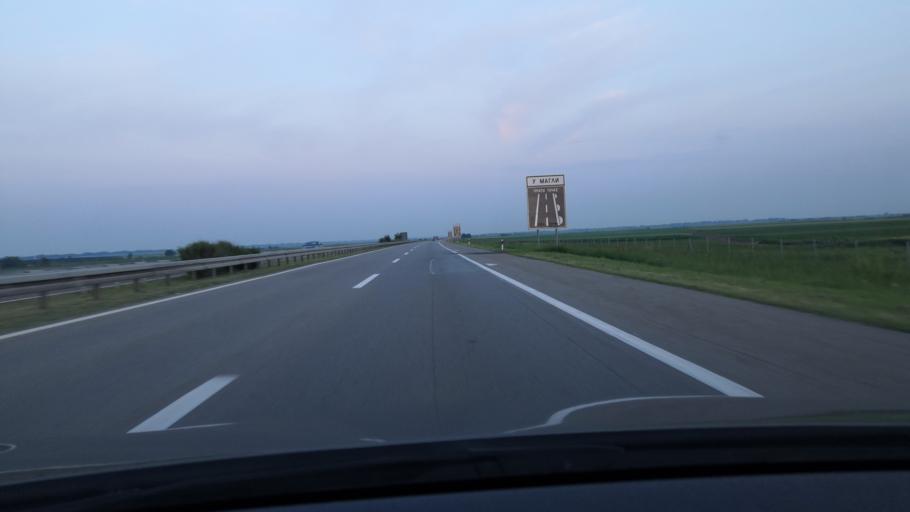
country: RS
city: Novi Karlovci
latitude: 45.0648
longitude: 20.1581
